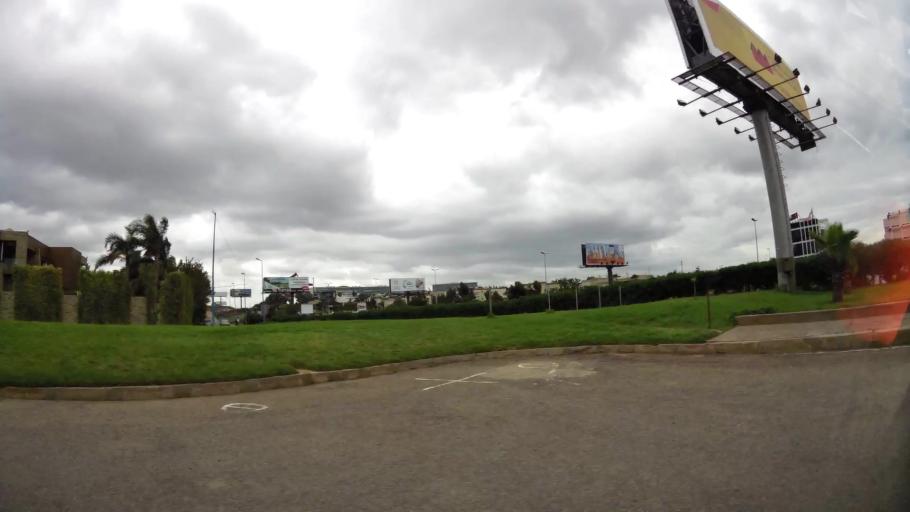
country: MA
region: Grand Casablanca
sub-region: Casablanca
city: Casablanca
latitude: 33.5355
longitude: -7.6385
